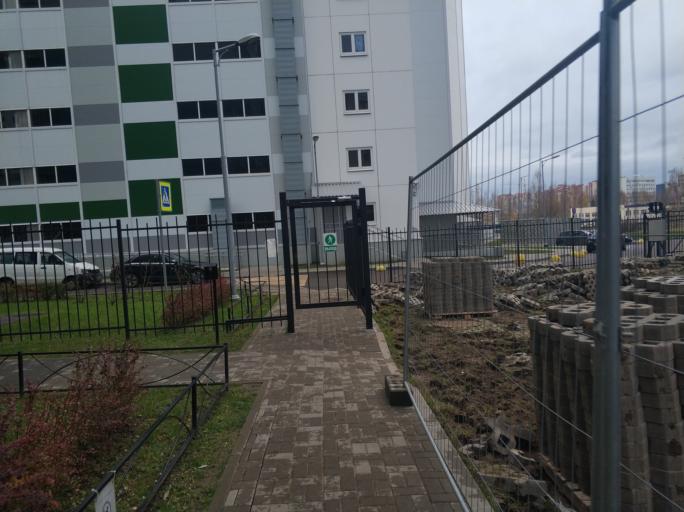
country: RU
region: Leningrad
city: Murino
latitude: 60.0535
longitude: 30.4509
